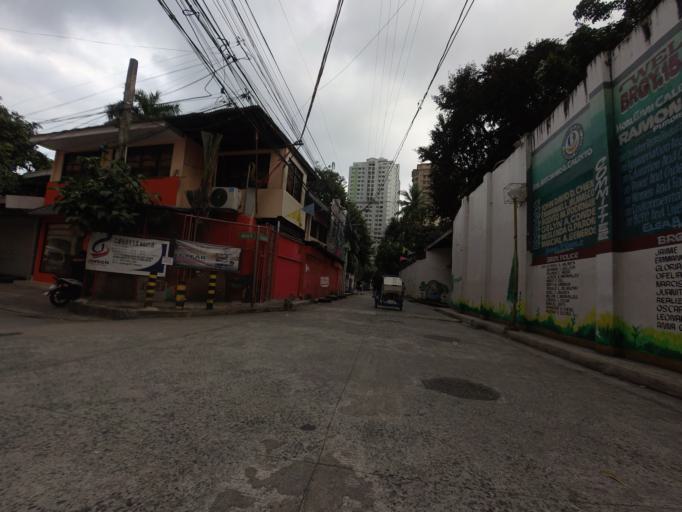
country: PH
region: Metro Manila
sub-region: City of Manila
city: Port Area
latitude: 14.5598
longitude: 120.9929
